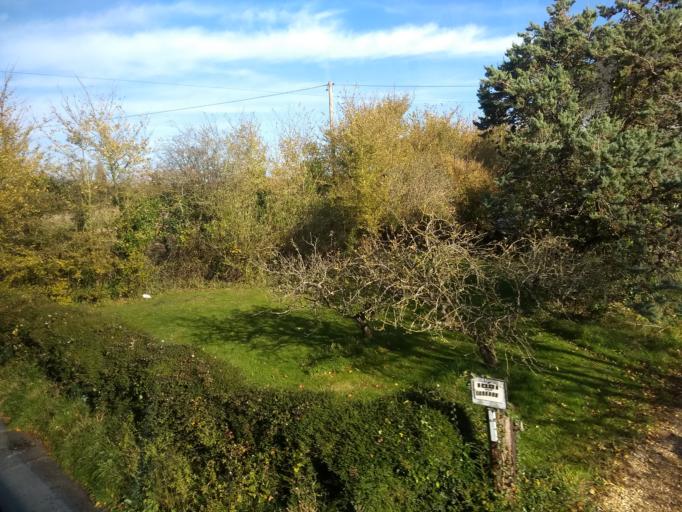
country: GB
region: England
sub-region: Isle of Wight
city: Shalfleet
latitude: 50.6919
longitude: -1.4322
